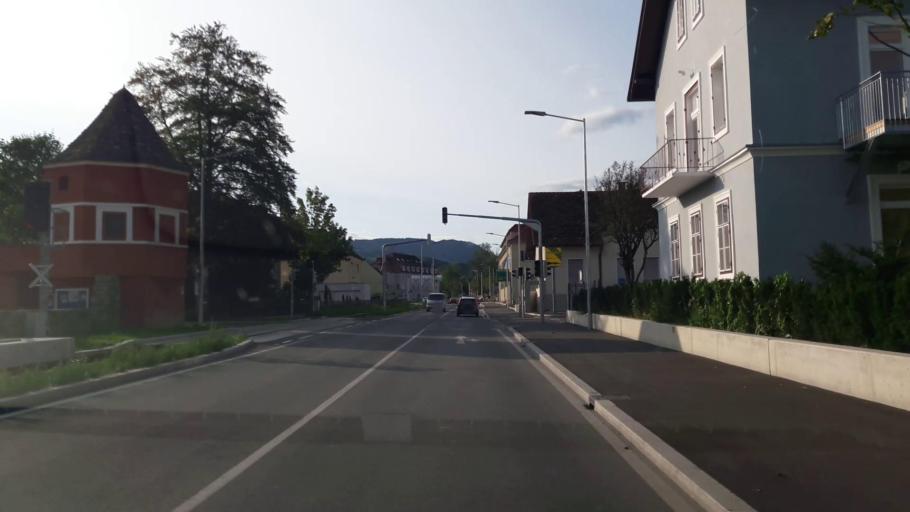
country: AT
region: Styria
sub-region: Politischer Bezirk Weiz
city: Weiz
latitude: 47.2197
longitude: 15.6267
